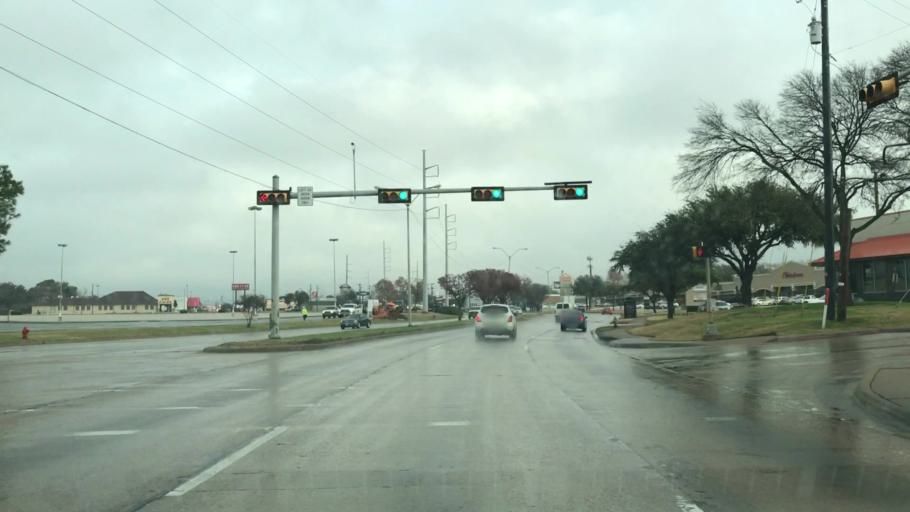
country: US
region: Texas
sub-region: Dallas County
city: Irving
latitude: 32.8407
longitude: -96.9933
